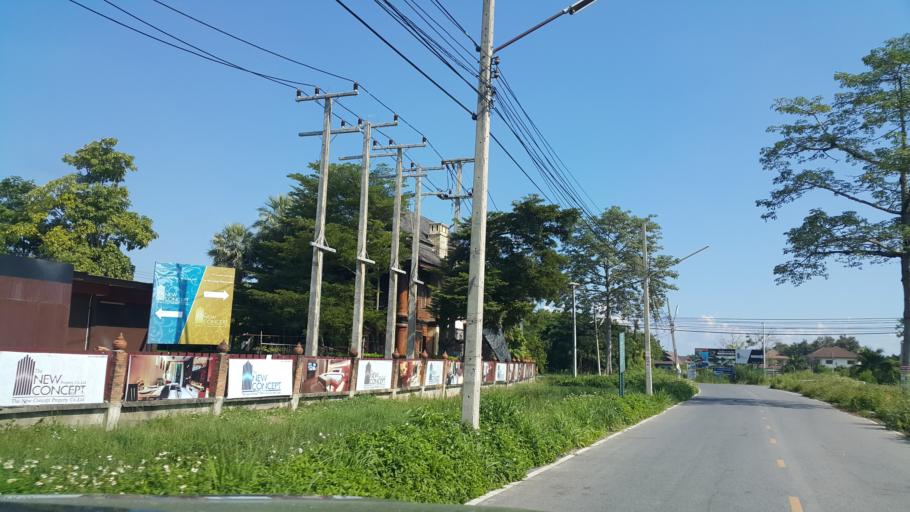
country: TH
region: Chiang Mai
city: Hang Dong
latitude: 18.7330
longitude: 98.9589
